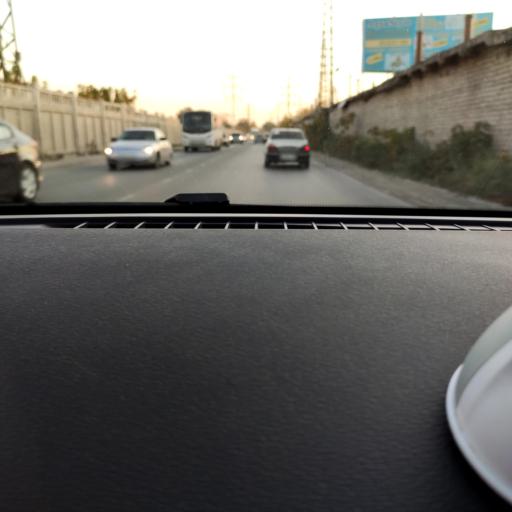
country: RU
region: Samara
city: Petra-Dubrava
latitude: 53.2476
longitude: 50.2930
